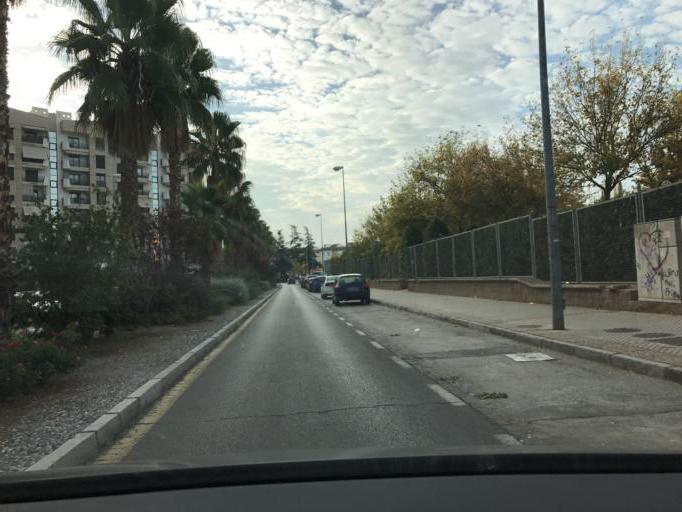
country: ES
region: Andalusia
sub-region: Provincia de Granada
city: Maracena
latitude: 37.1945
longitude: -3.6244
